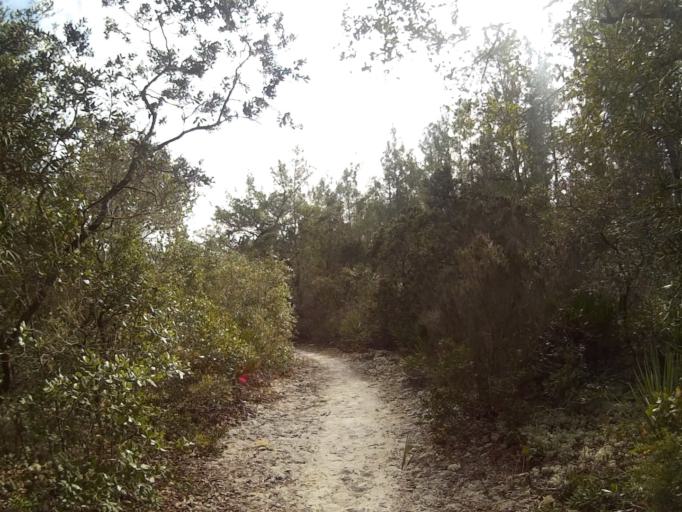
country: US
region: Florida
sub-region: Lake County
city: Astor
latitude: 29.0707
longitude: -81.6204
